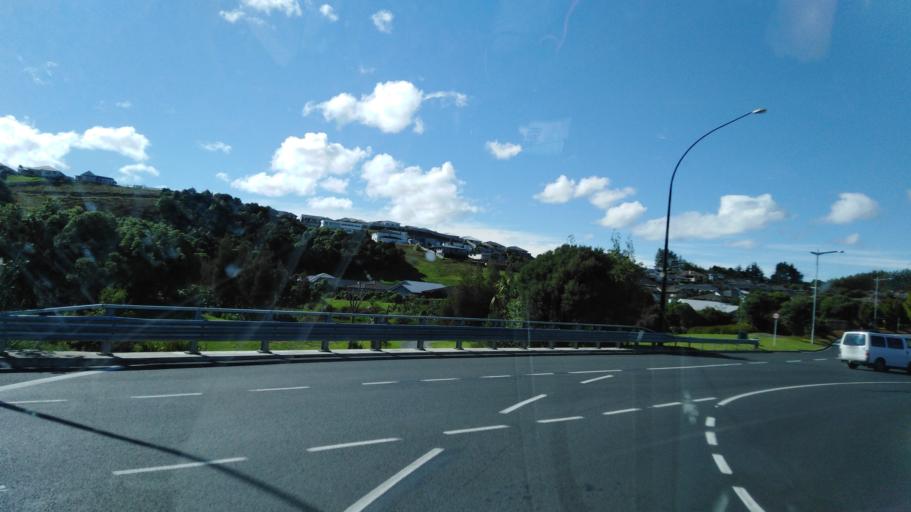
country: NZ
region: Bay of Plenty
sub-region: Tauranga City
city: Tauranga
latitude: -37.7383
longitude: 176.1082
